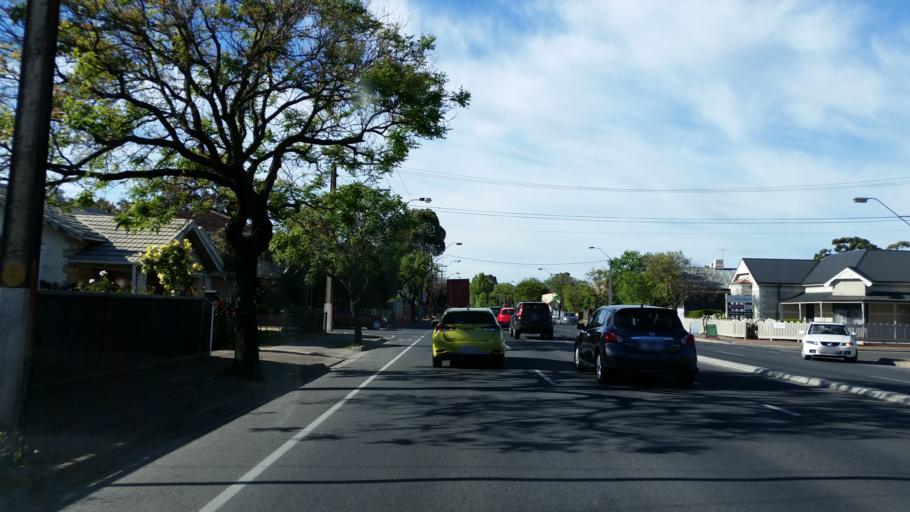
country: AU
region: South Australia
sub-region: Norwood Payneham St Peters
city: Payneham
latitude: -34.8998
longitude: 138.6395
